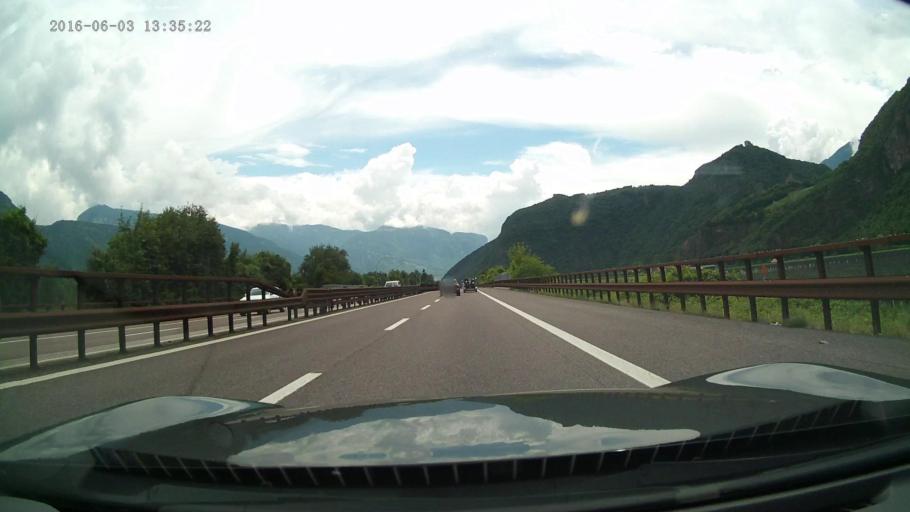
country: IT
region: Trentino-Alto Adige
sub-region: Bolzano
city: Vadena
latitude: 46.3896
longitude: 11.2941
